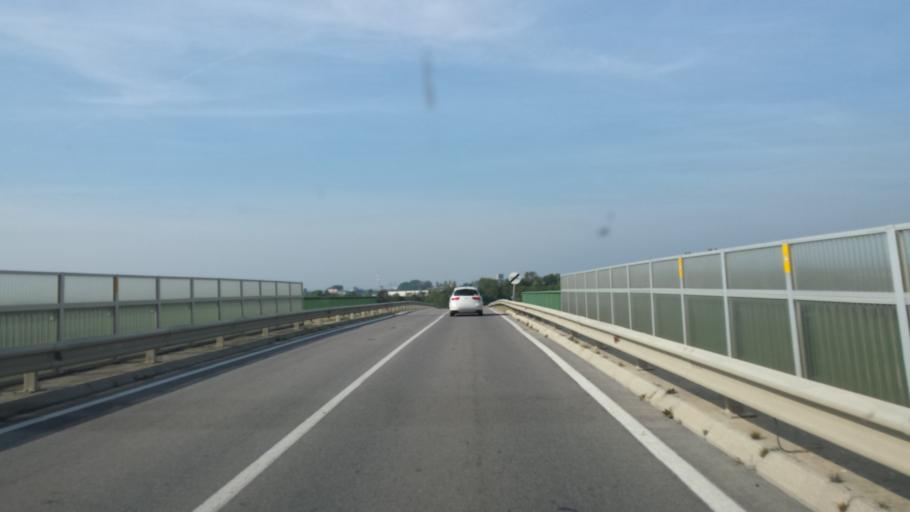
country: AT
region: Lower Austria
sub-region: Politischer Bezirk Tulln
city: Tulln
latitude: 48.3156
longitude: 16.0375
